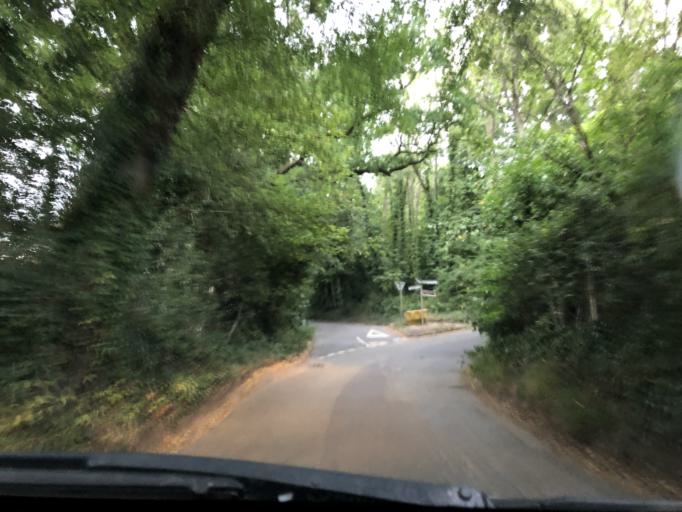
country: GB
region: England
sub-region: Kent
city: Sevenoaks
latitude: 51.2415
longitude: 0.2309
